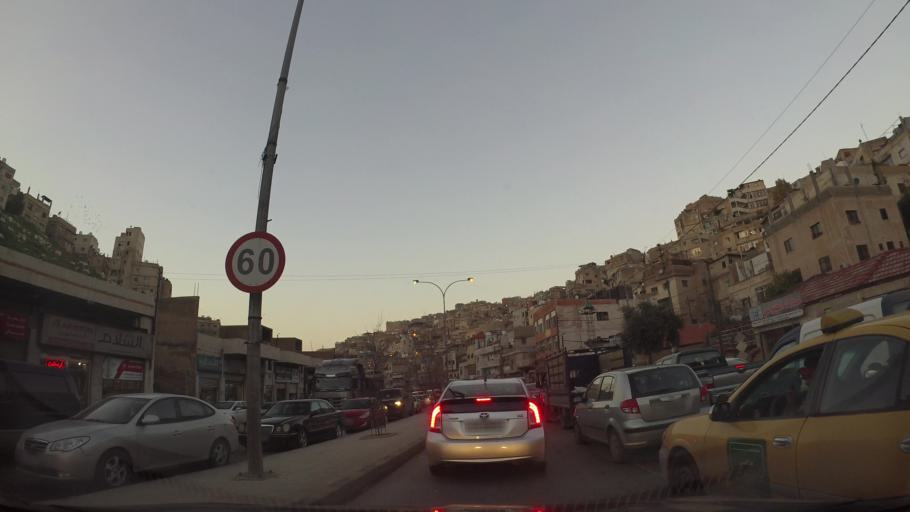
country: JO
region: Amman
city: Amman
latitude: 31.9373
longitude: 35.9237
